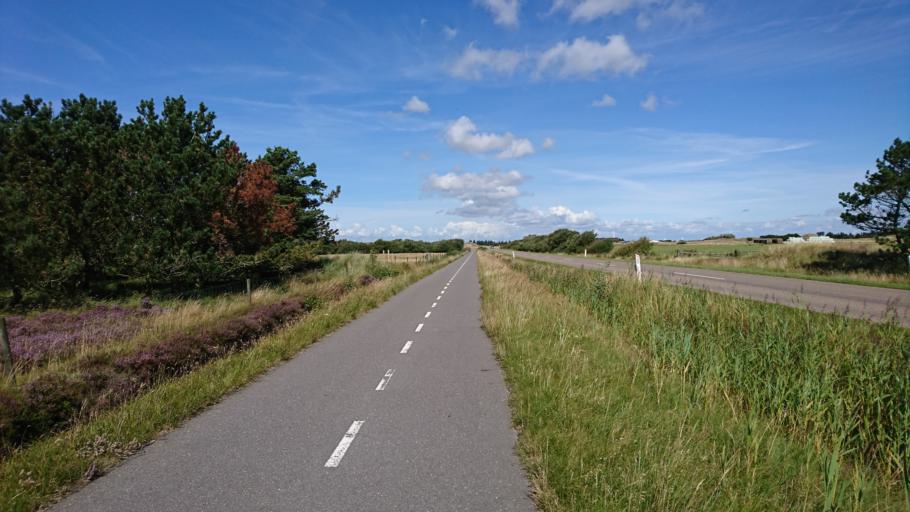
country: DK
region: South Denmark
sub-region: Fano Kommune
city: Nordby
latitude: 55.3629
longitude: 8.4576
